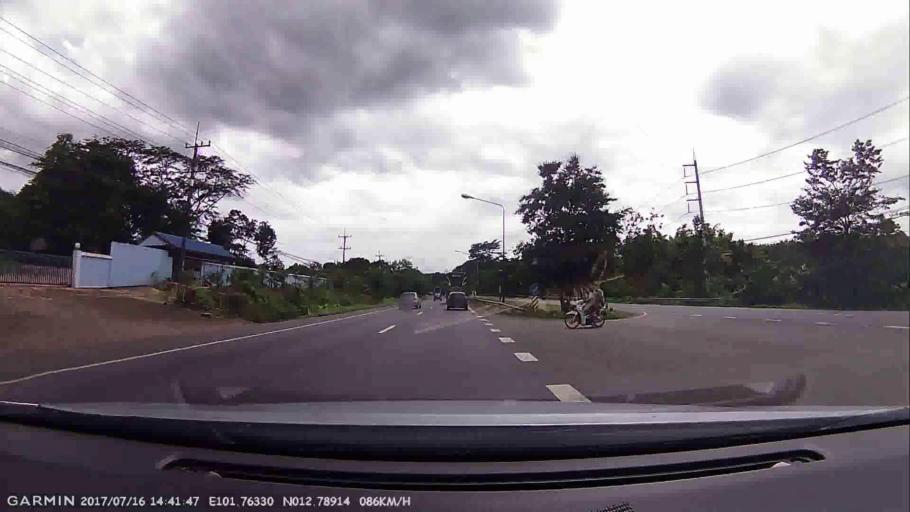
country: TH
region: Chanthaburi
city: Na Yai Am
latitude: 12.7891
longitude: 101.7630
